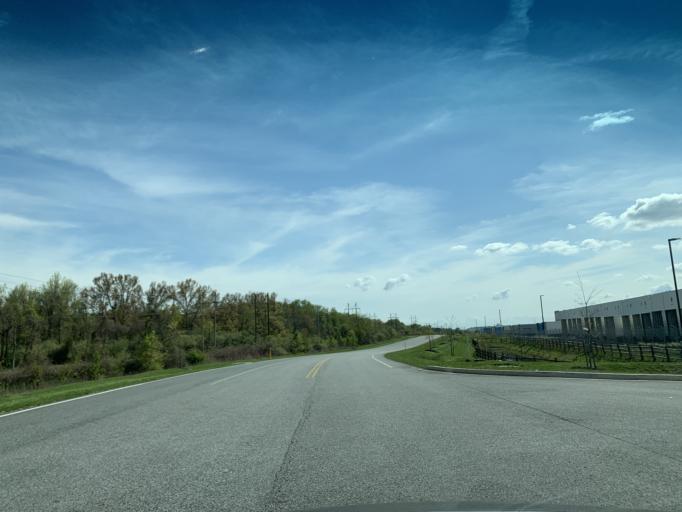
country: US
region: Maryland
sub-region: Harford County
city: Perryman
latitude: 39.4815
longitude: -76.1798
